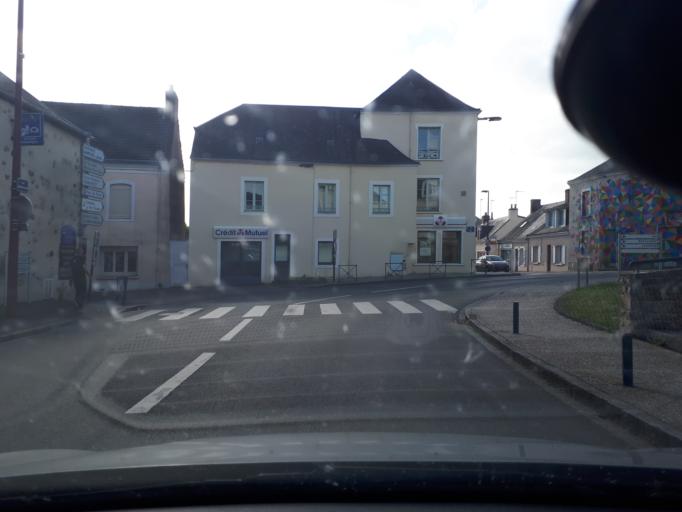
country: FR
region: Pays de la Loire
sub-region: Departement de la Sarthe
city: Change
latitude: 48.0142
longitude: 0.2715
